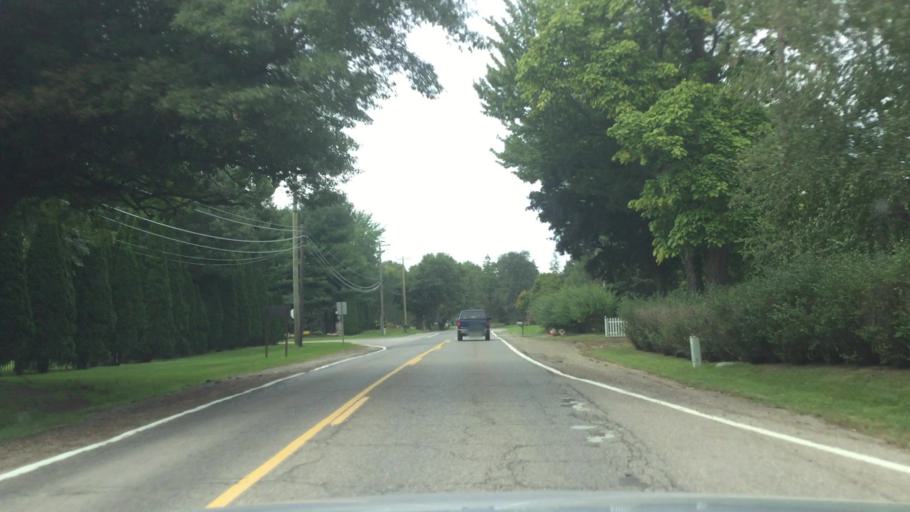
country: US
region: Michigan
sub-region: Oakland County
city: Clarkston
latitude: 42.7591
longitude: -83.4843
